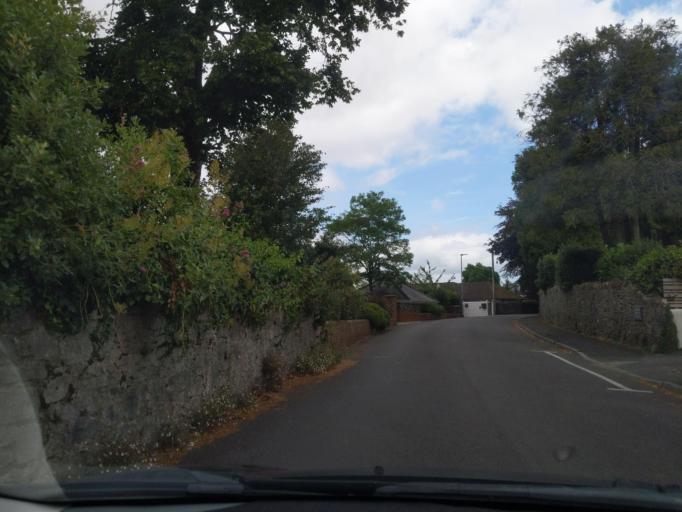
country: GB
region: England
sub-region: Devon
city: Totnes
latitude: 50.4337
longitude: -3.6725
